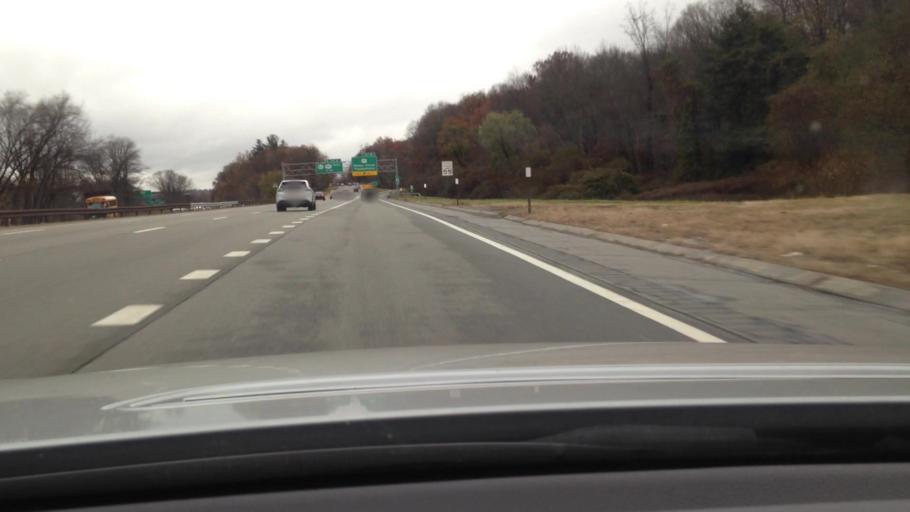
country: US
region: New York
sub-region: Westchester County
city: Hawthorne
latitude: 41.1165
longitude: -73.8059
